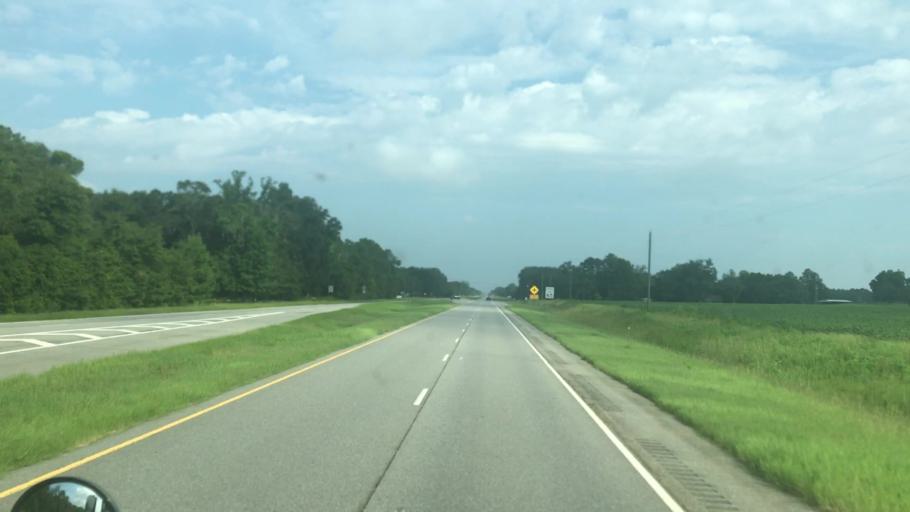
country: US
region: Georgia
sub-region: Early County
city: Blakely
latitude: 31.2772
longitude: -84.8336
